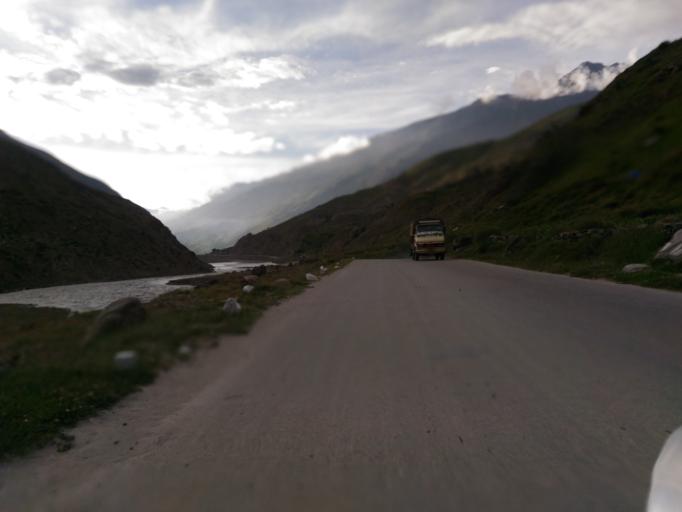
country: IN
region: Himachal Pradesh
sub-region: Lahul and Spiti
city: Kyelang
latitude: 32.4504
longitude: 77.1527
